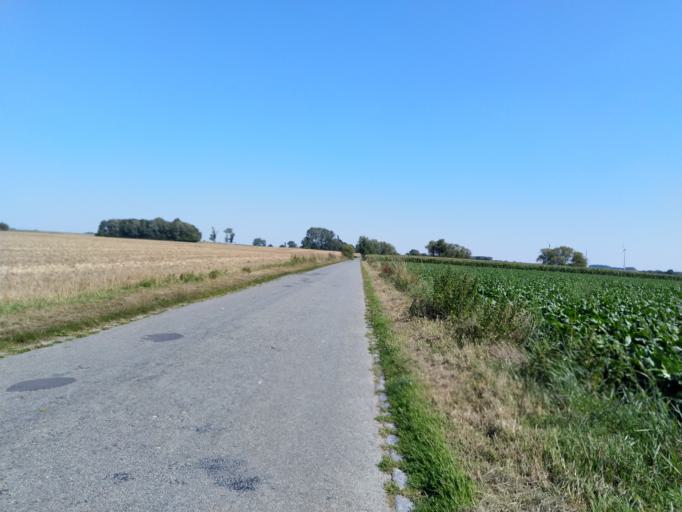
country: BE
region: Wallonia
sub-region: Province du Hainaut
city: Roeulx
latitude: 50.4907
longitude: 4.0409
